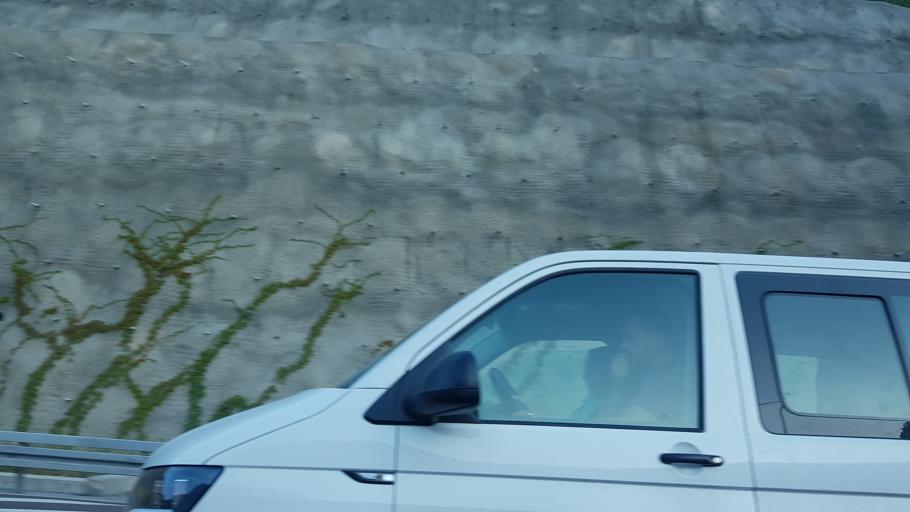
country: TR
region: Bursa
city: Yenikoy
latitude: 40.5847
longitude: 29.3628
